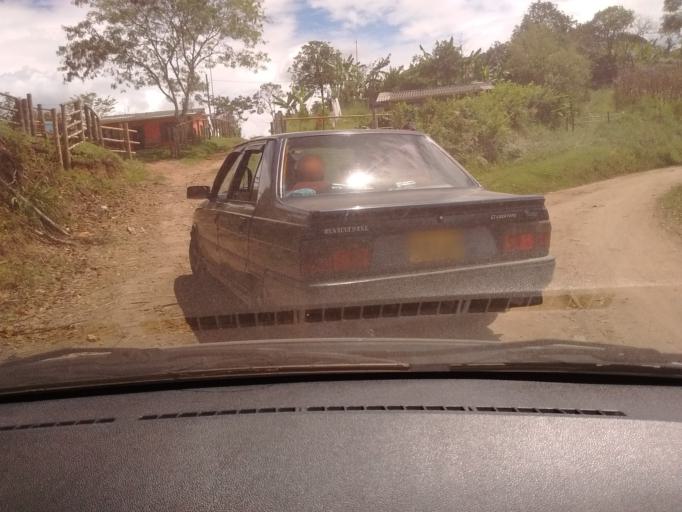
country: CO
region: Cauca
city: El Tambo
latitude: 2.4730
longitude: -76.8312
